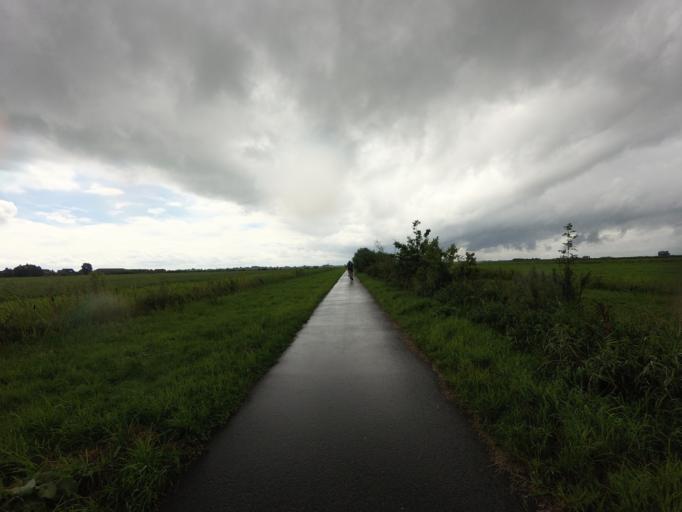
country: NL
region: North Holland
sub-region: Gemeente Wijdemeren
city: Nieuw-Loosdrecht
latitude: 52.1713
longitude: 5.1457
